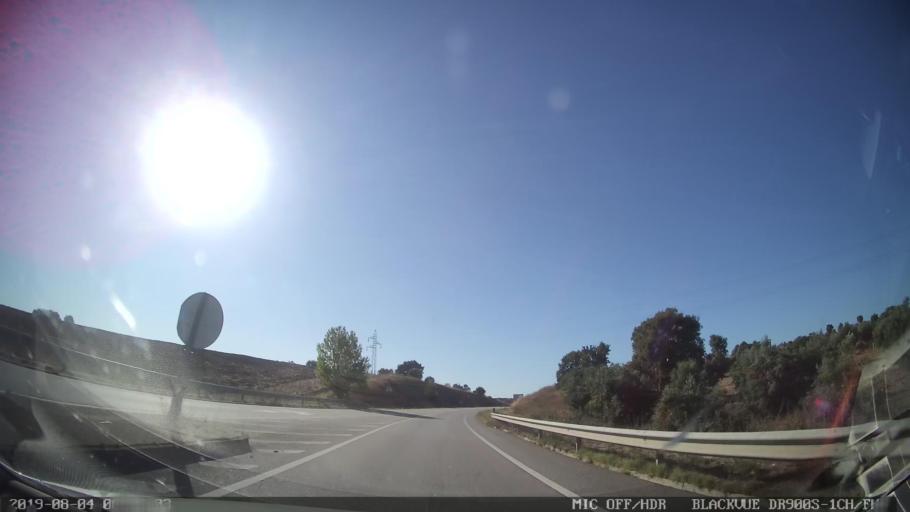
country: PT
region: Santarem
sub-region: Abrantes
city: Alferrarede
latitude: 39.4867
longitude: -8.0972
